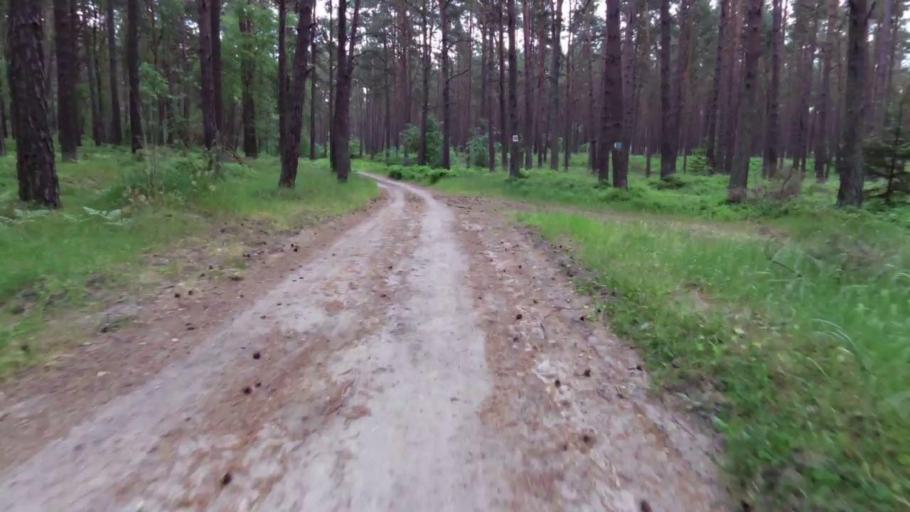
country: PL
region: West Pomeranian Voivodeship
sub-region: Swinoujscie
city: Swinoujscie
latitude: 53.9017
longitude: 14.3425
